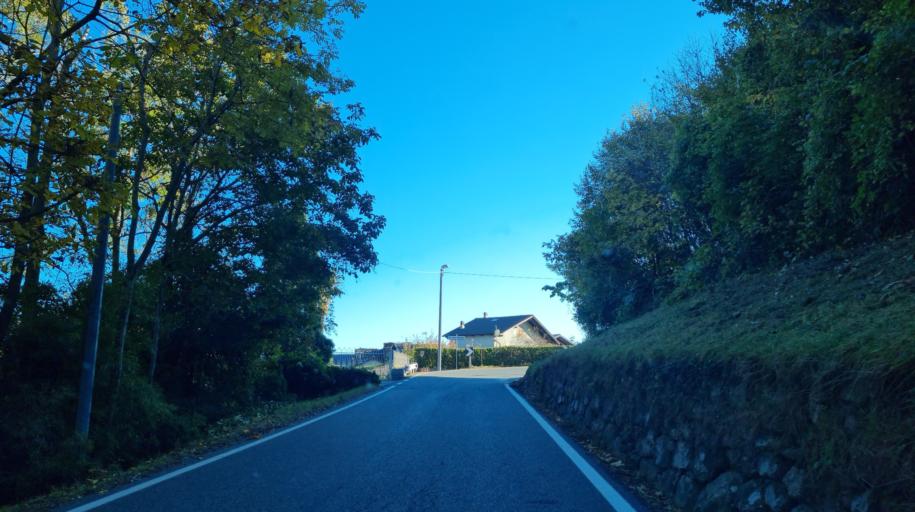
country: IT
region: Piedmont
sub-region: Provincia di Torino
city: Lessolo
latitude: 45.4640
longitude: 7.8034
